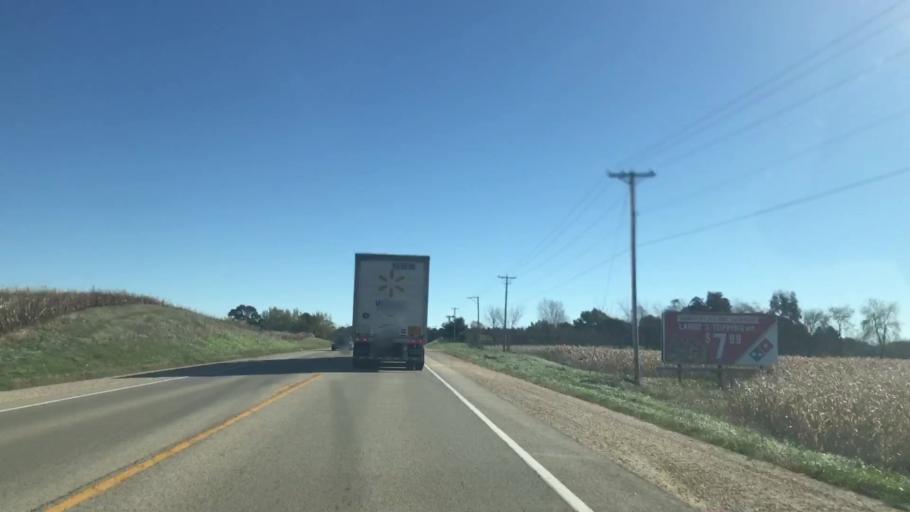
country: US
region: Wisconsin
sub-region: Dodge County
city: Juneau
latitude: 43.4448
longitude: -88.7143
